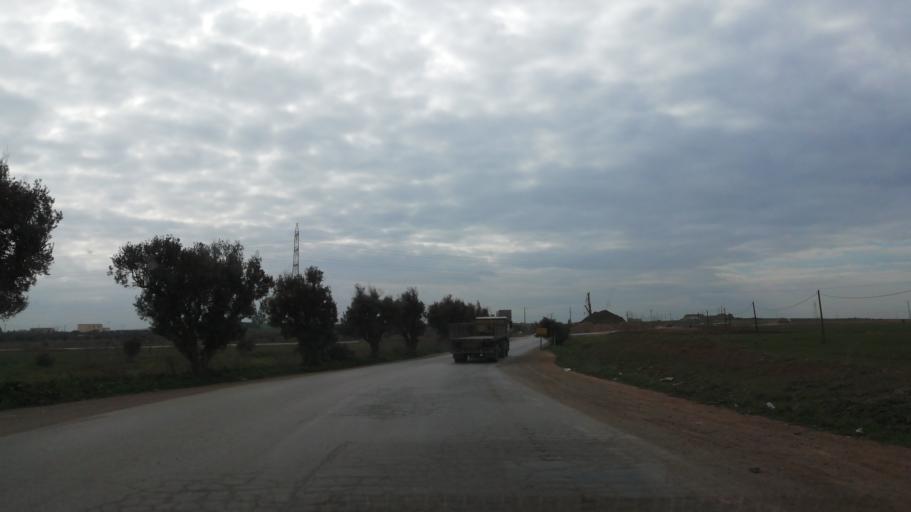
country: DZ
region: Oran
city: Ain el Bya
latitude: 35.7927
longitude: -0.3416
